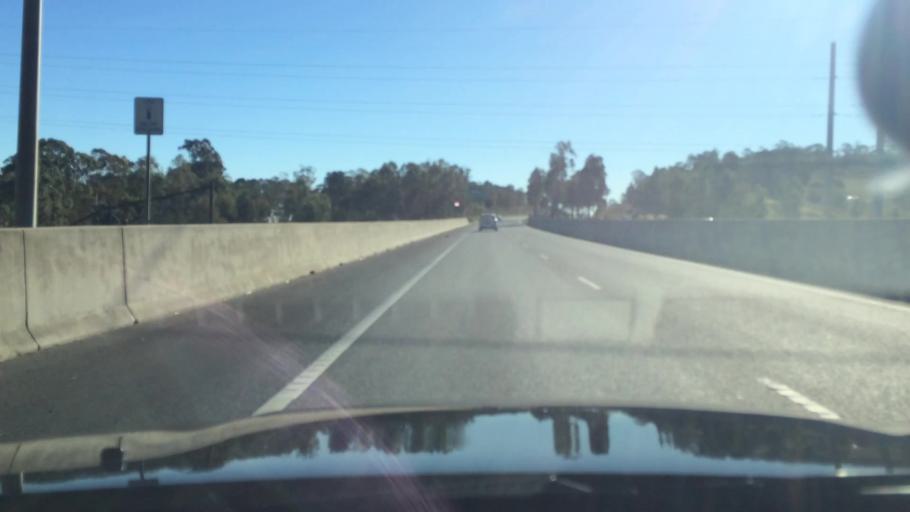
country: AU
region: New South Wales
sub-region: Fairfield
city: Cecil Park
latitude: -33.8670
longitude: 150.8467
